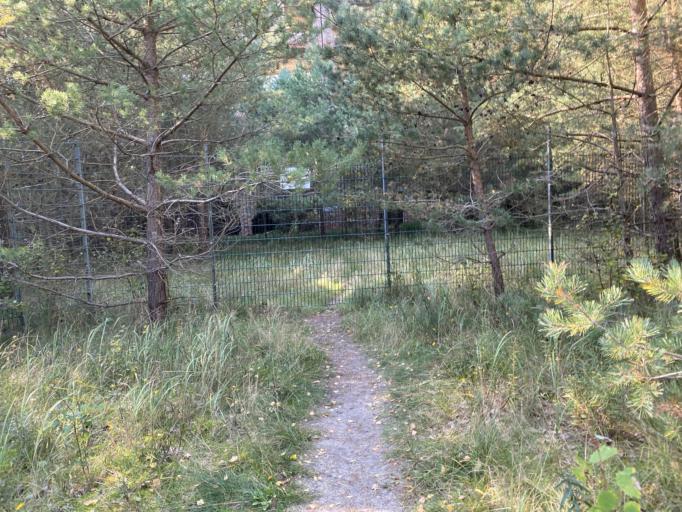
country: DE
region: Mecklenburg-Vorpommern
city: Sagard
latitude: 54.4572
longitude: 13.5685
